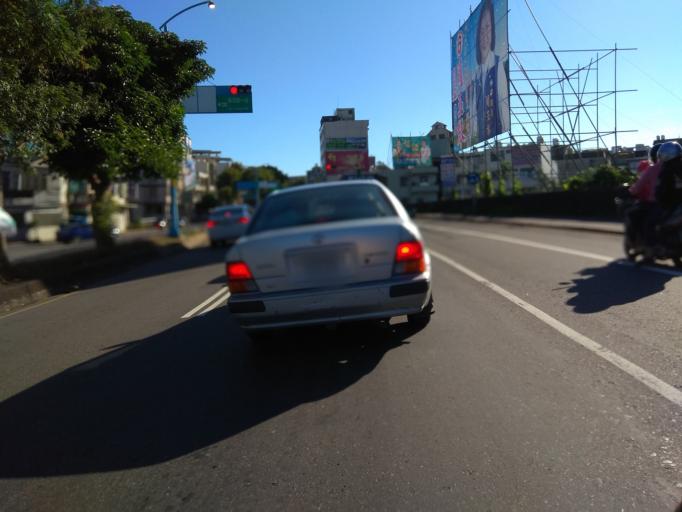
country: TW
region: Taiwan
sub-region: Hsinchu
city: Zhubei
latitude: 24.9061
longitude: 121.1410
